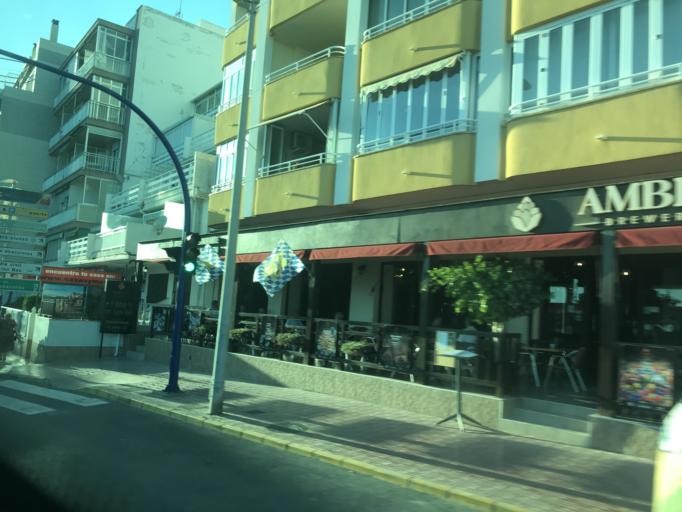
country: ES
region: Valencia
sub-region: Provincia de Alicante
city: Torrevieja
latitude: 37.9808
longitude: -0.6639
